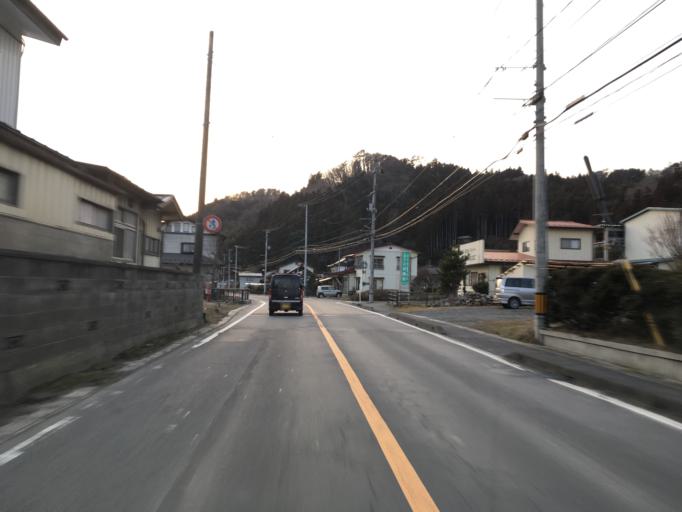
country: JP
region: Fukushima
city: Ishikawa
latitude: 37.0294
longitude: 140.3695
